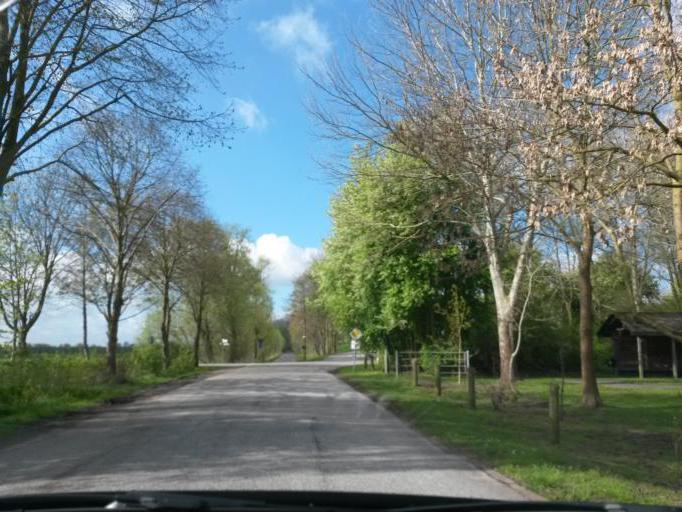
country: DE
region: Schleswig-Holstein
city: Hetlingen
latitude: 53.6026
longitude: 9.6299
